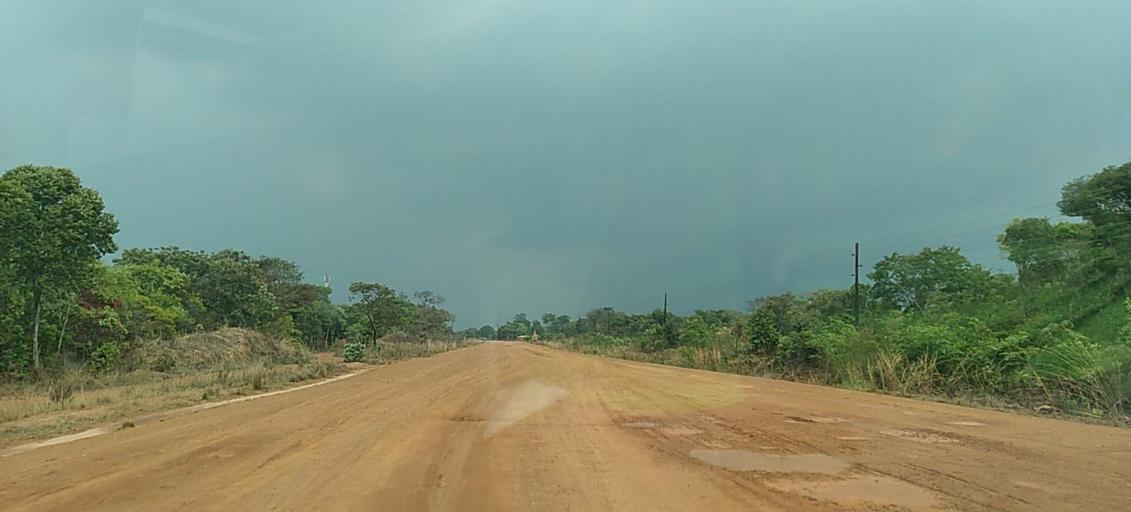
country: ZM
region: North-Western
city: Mwinilunga
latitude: -11.6469
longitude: 24.3995
